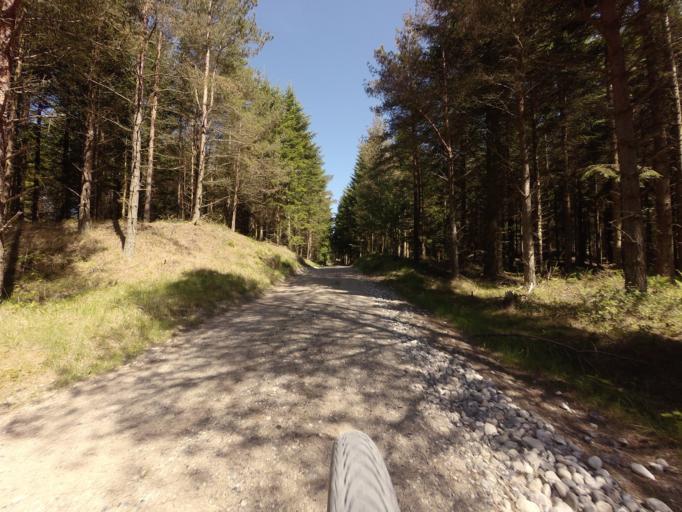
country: DK
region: North Denmark
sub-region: Jammerbugt Kommune
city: Pandrup
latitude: 57.2415
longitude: 9.6029
